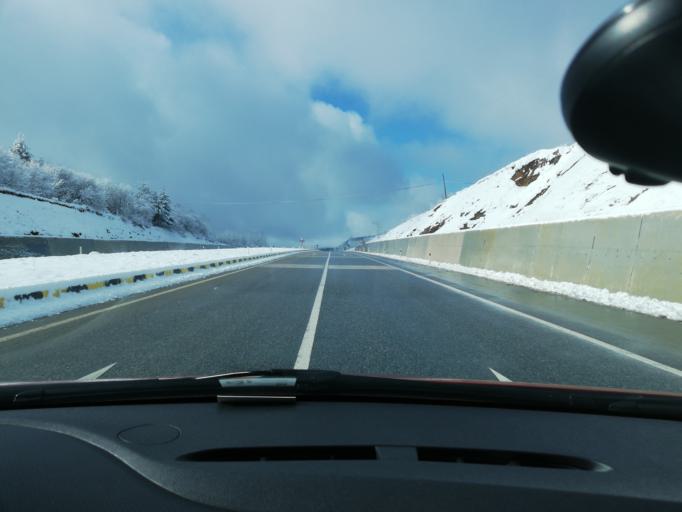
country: TR
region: Kastamonu
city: Kuzyaka
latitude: 41.3332
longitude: 33.6227
